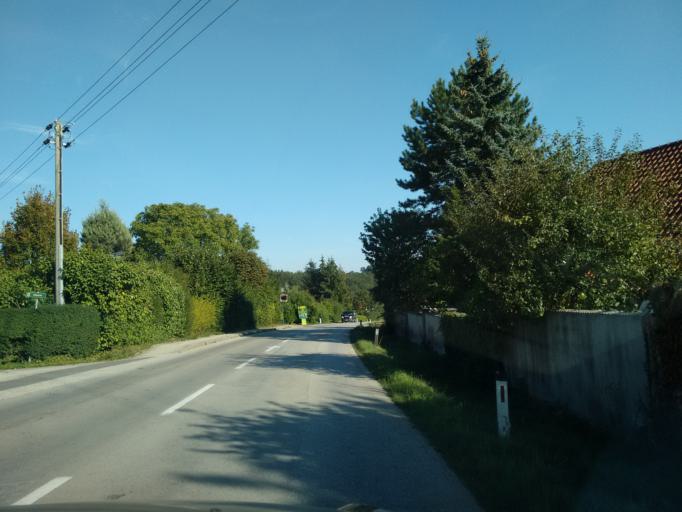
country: AT
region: Upper Austria
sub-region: Wels-Land
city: Marchtrenk
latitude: 48.1525
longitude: 14.1748
